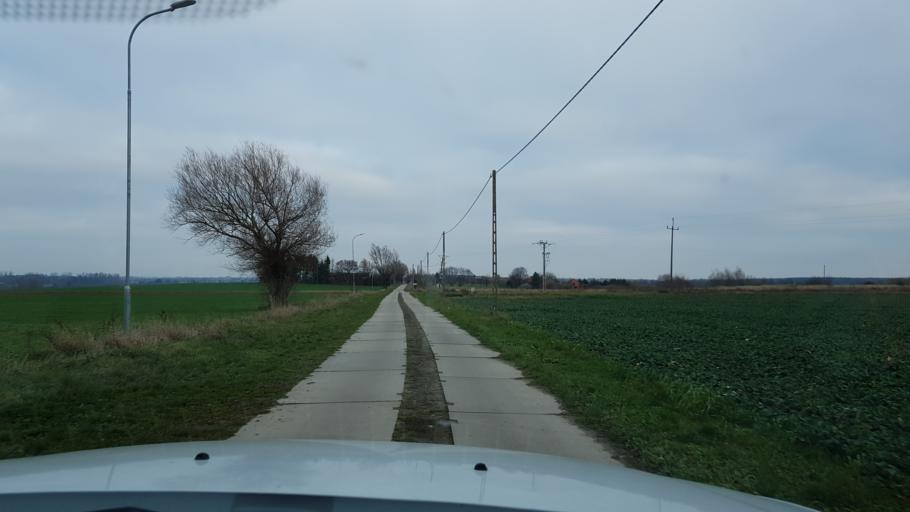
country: PL
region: West Pomeranian Voivodeship
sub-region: Powiat kolobrzeski
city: Grzybowo
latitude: 54.1192
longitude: 15.5379
